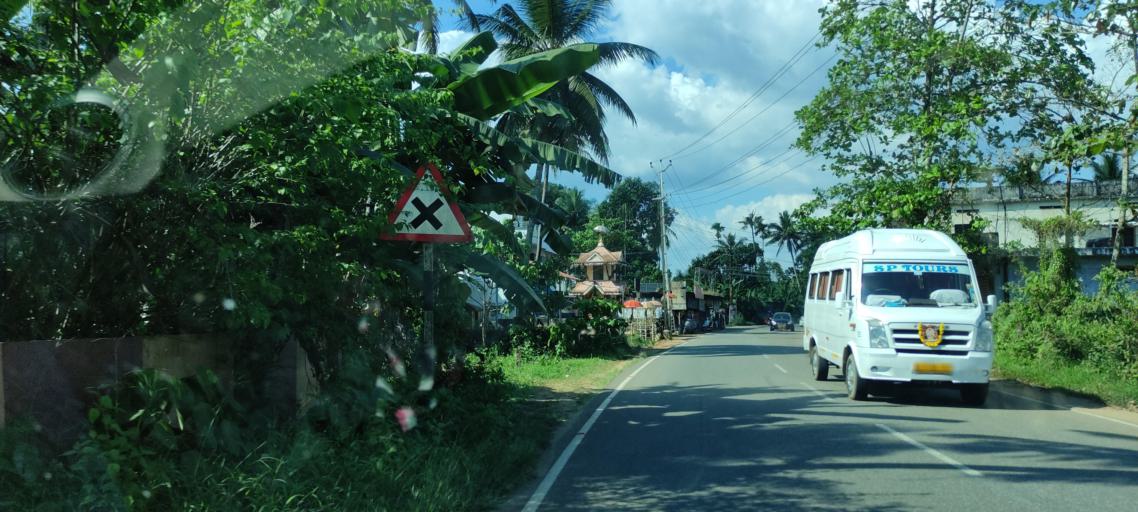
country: IN
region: Kerala
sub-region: Pattanamtitta
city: Adur
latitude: 9.2085
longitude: 76.7463
